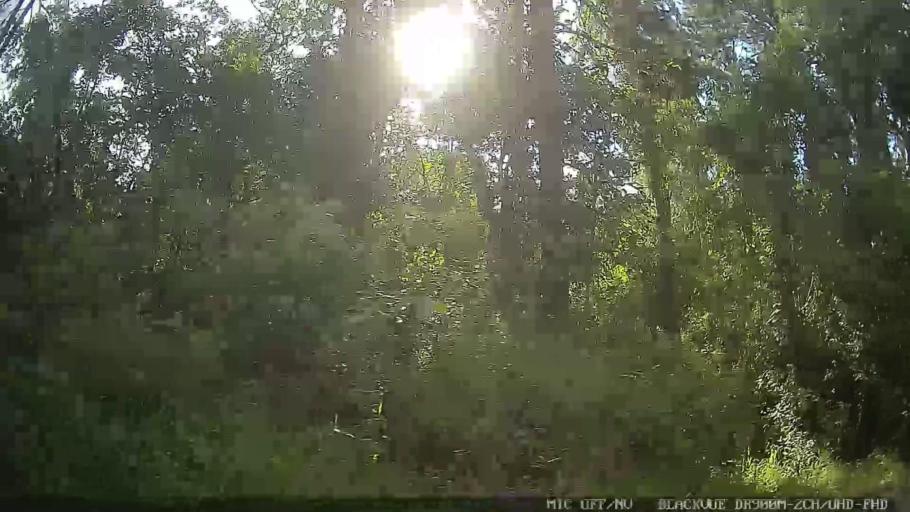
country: BR
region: Sao Paulo
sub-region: Bom Jesus Dos Perdoes
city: Bom Jesus dos Perdoes
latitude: -23.1665
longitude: -46.5129
